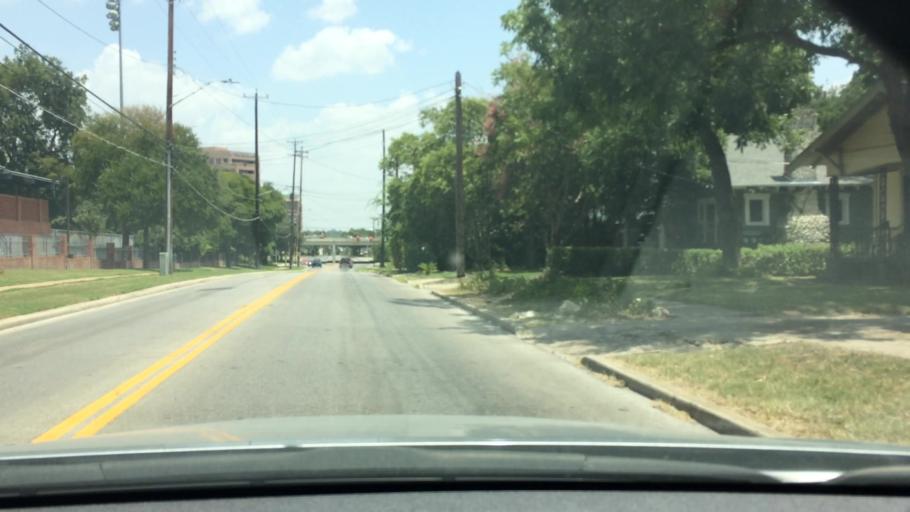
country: US
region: Texas
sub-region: Bexar County
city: Olmos Park
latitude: 29.4568
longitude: -98.4843
